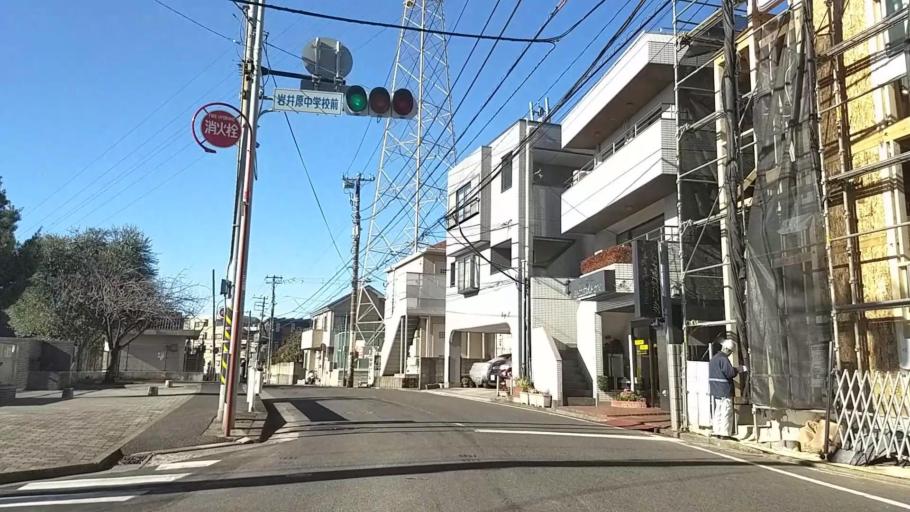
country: JP
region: Kanagawa
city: Yokohama
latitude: 35.4442
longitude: 139.6019
